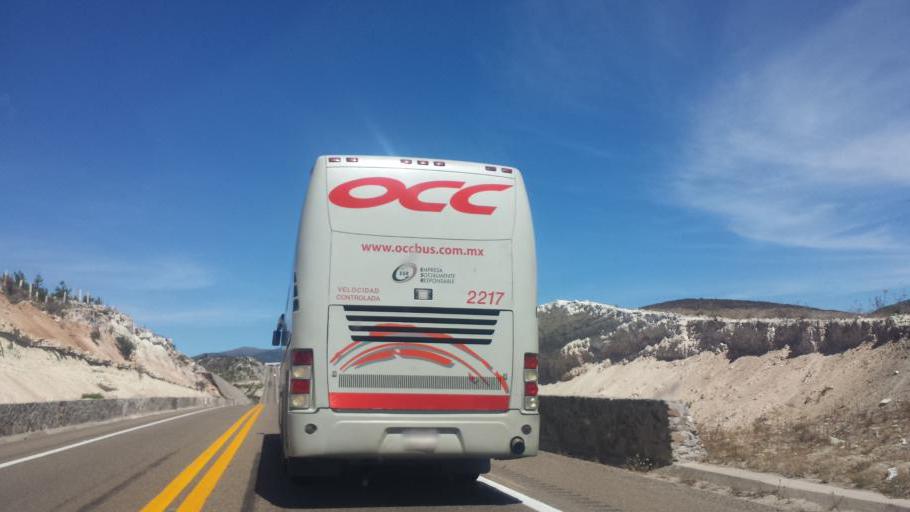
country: MX
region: Oaxaca
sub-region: Villa Tejupam de la Union
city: Villa Tejupam de la Union
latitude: 17.9052
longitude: -97.3658
